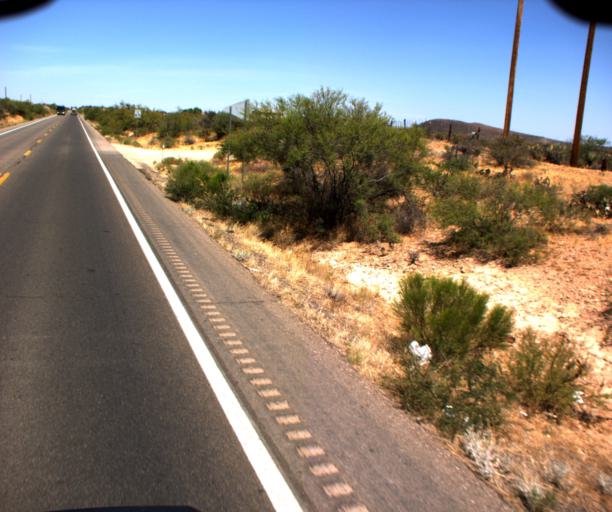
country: US
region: Arizona
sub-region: Gila County
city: Peridot
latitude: 33.3036
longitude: -110.4785
